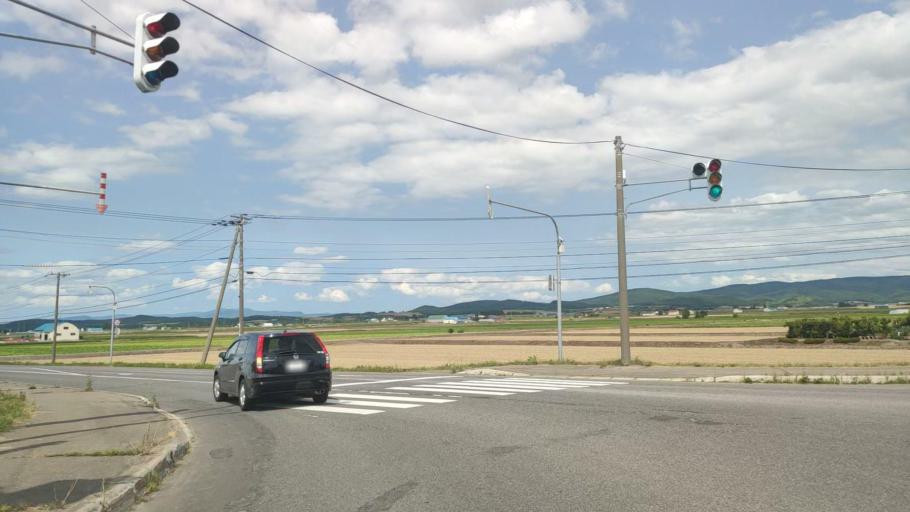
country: JP
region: Hokkaido
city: Nayoro
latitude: 44.1910
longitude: 142.4158
